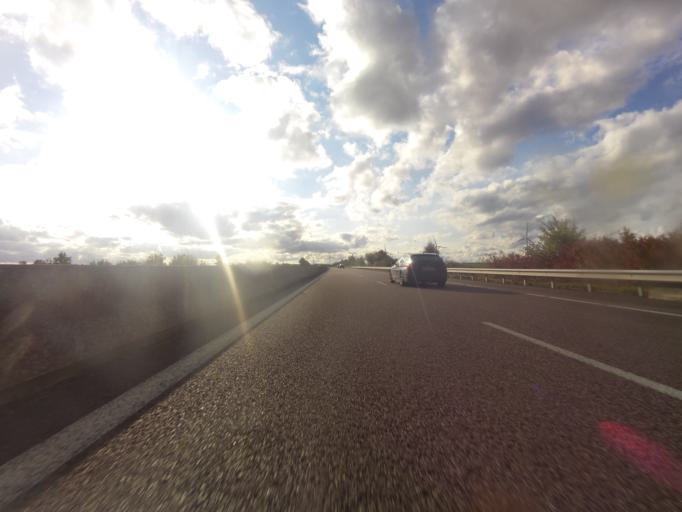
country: FR
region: Picardie
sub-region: Departement de la Somme
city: Hornoy-le-Bourg
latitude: 49.8115
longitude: 1.8467
